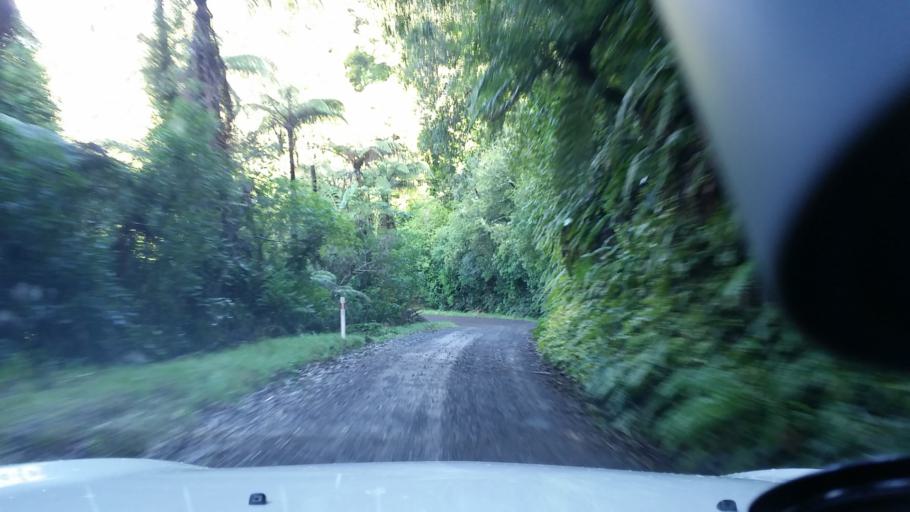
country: NZ
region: Bay of Plenty
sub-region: Kawerau District
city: Kawerau
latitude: -38.0253
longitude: 176.5607
